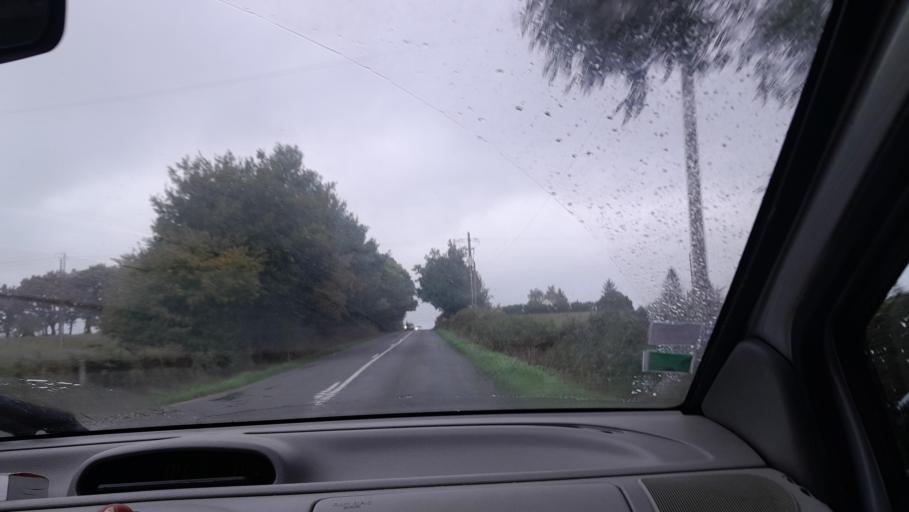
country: FR
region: Pays de la Loire
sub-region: Departement de la Mayenne
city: Congrier
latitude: 47.8653
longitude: -1.1314
